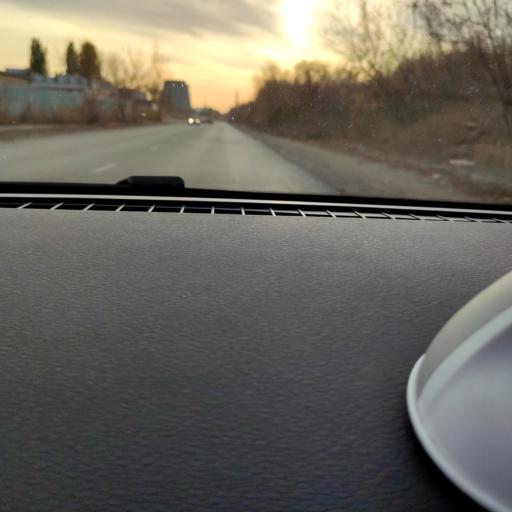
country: RU
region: Samara
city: Petra-Dubrava
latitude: 53.2556
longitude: 50.2805
